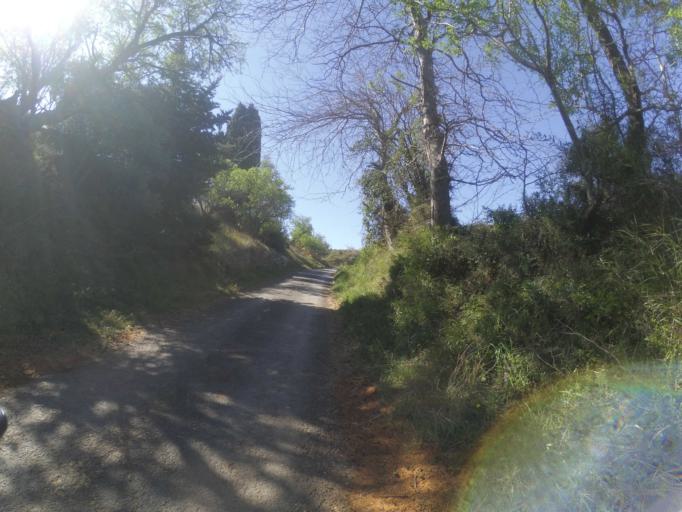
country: FR
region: Languedoc-Roussillon
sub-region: Departement des Pyrenees-Orientales
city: Baixas
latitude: 42.7414
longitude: 2.7982
